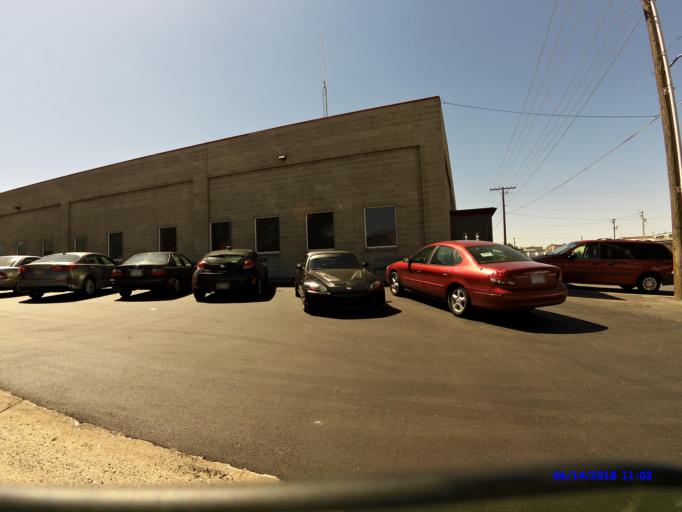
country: US
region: Utah
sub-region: Weber County
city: Ogden
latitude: 41.2134
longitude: -112.0063
